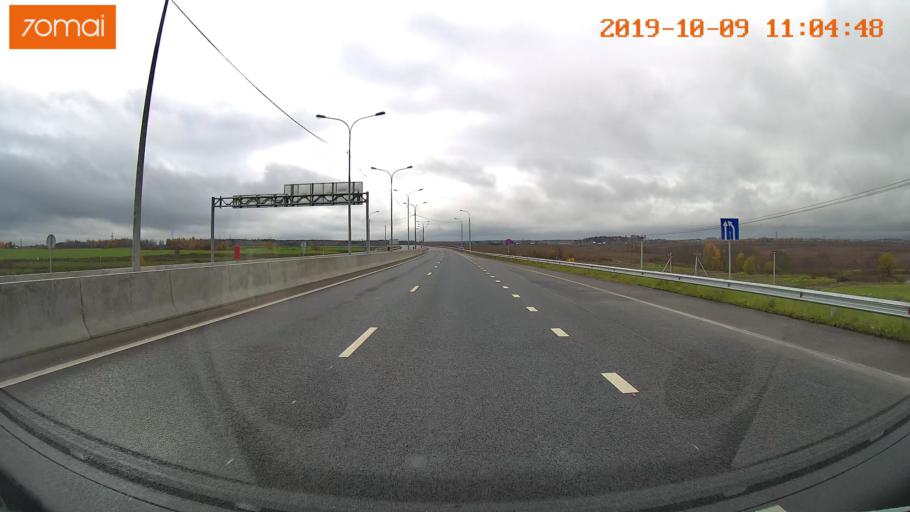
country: RU
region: Vologda
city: Molochnoye
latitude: 59.2078
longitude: 39.7634
